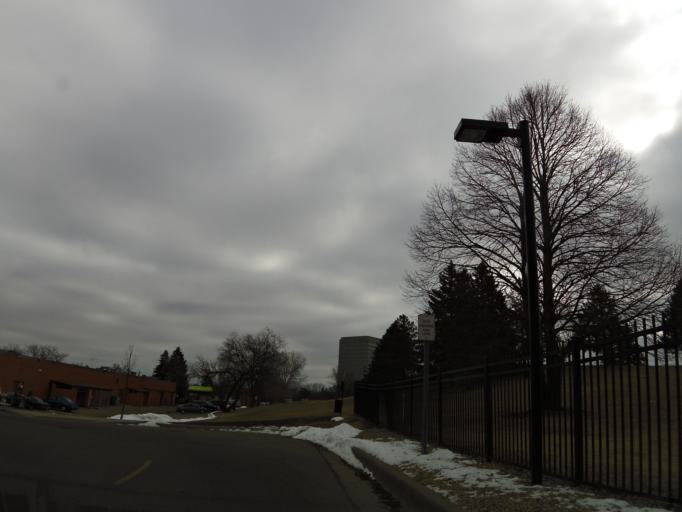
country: US
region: Minnesota
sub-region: Hennepin County
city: Bloomington
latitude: 44.8569
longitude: -93.3066
